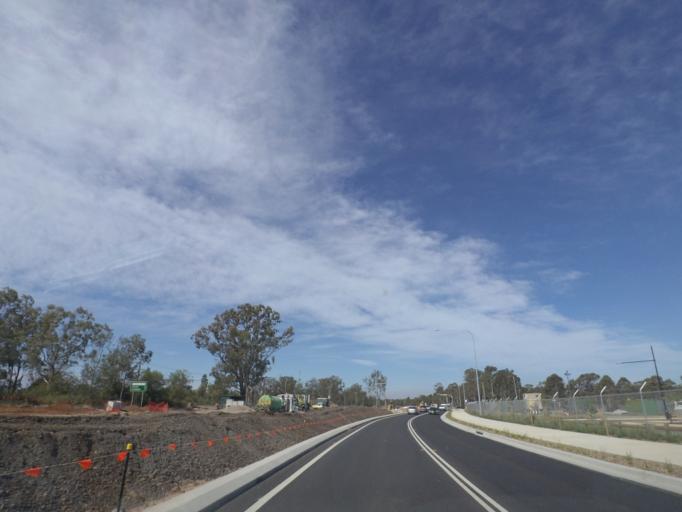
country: AU
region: New South Wales
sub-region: Campbelltown Municipality
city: Denham Court
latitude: -33.9727
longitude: 150.8616
